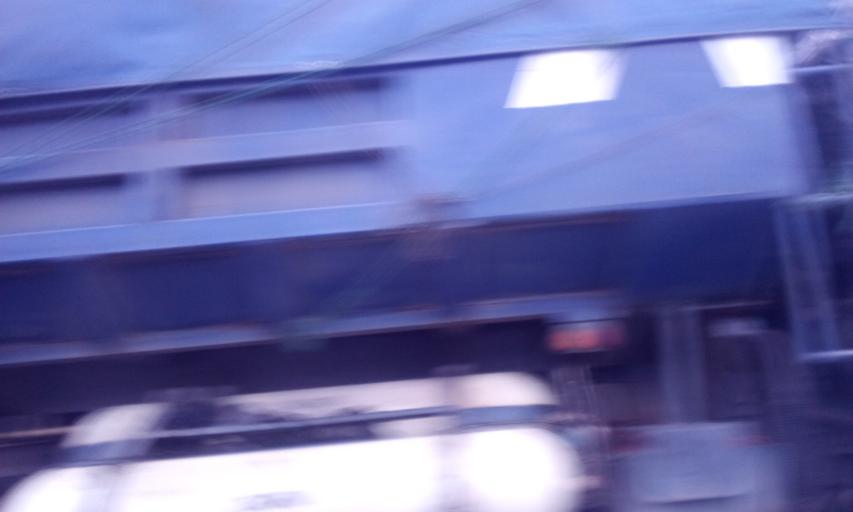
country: TH
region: Chon Buri
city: Ban Bueng
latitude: 13.2856
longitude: 101.2567
